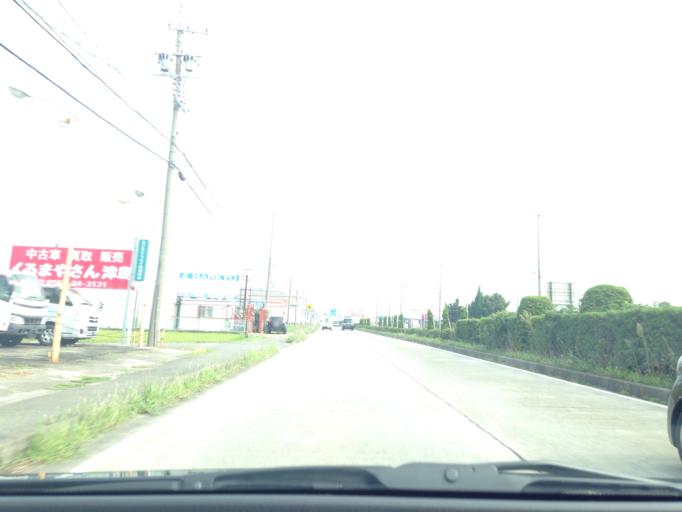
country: JP
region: Aichi
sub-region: Aisai-shi
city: Aisai
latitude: 35.1795
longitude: 136.7750
